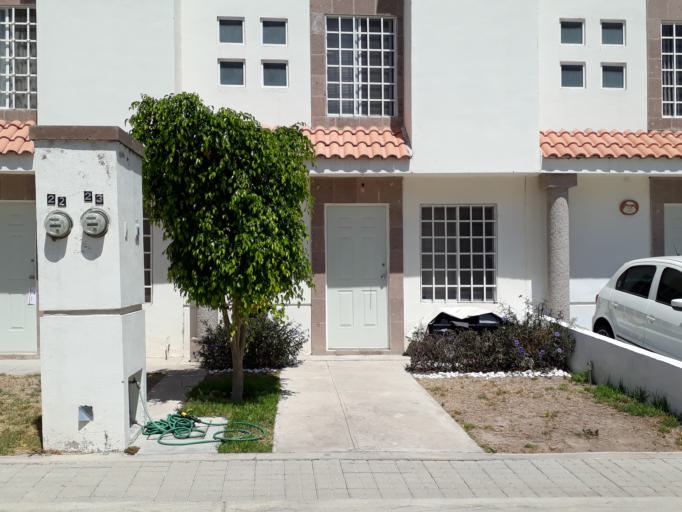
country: MX
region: Aguascalientes
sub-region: Aguascalientes
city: San Sebastian [Fraccionamiento]
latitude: 21.8099
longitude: -102.2965
